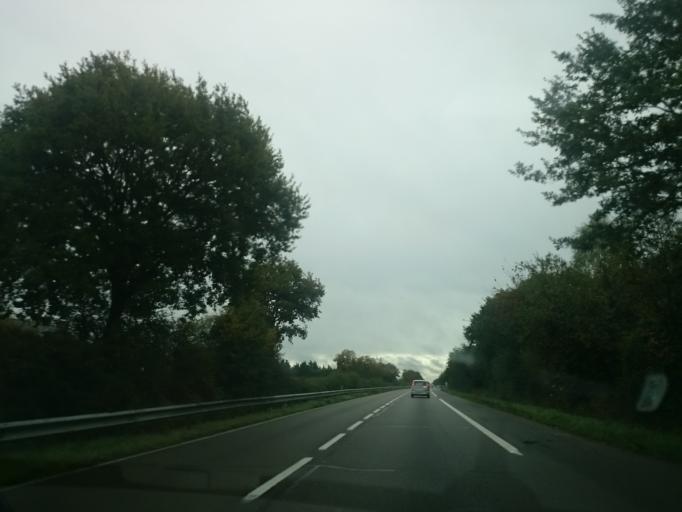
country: FR
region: Pays de la Loire
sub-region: Departement de la Loire-Atlantique
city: Malville
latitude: 47.3437
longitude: -1.8486
